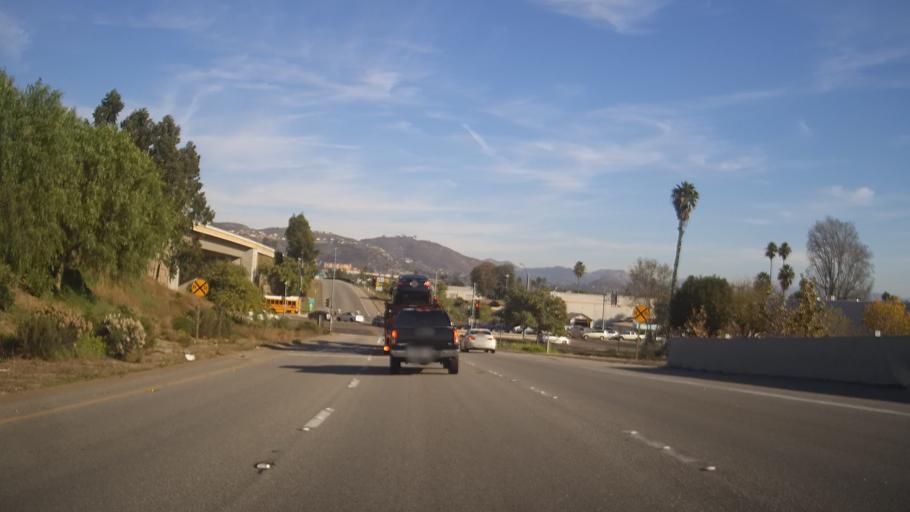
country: US
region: California
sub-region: San Diego County
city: Santee
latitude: 32.8327
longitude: -116.9851
